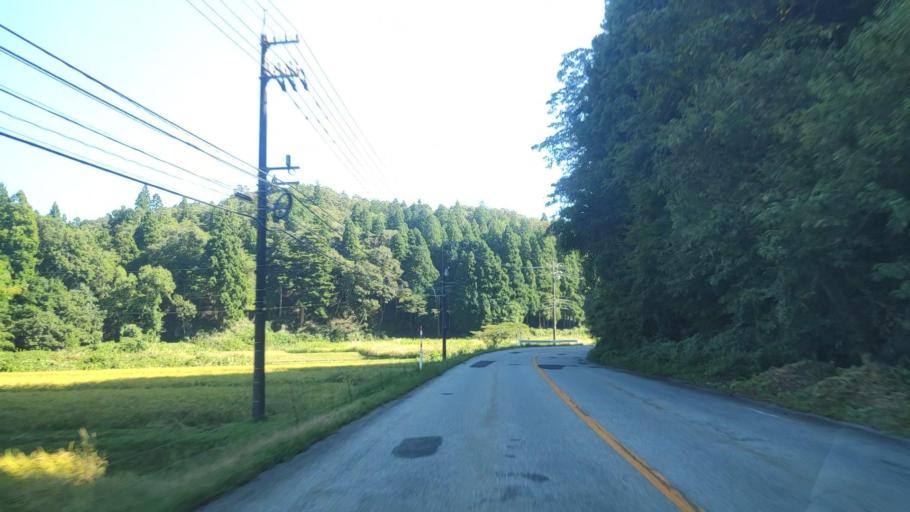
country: JP
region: Ishikawa
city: Nanao
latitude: 37.3315
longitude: 137.2084
